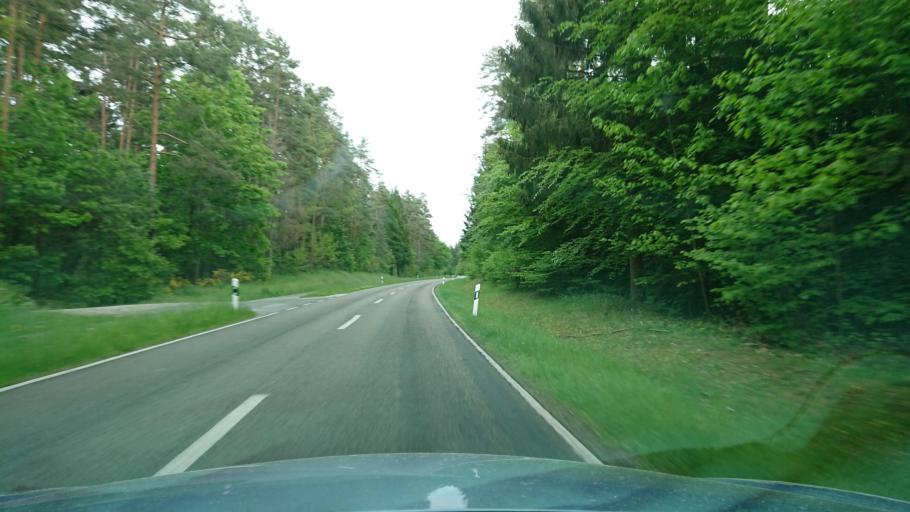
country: DE
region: Bavaria
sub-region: Regierungsbezirk Mittelfranken
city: Hemhofen
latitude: 49.6611
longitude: 10.9653
